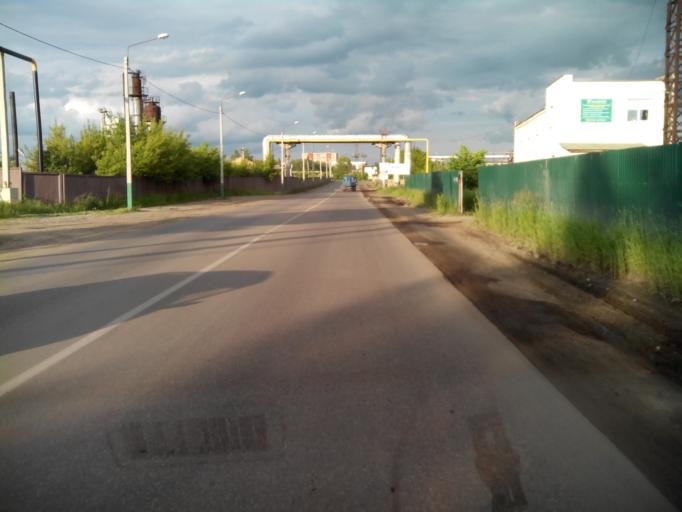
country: RU
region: Penza
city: Penza
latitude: 53.1311
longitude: 44.9936
